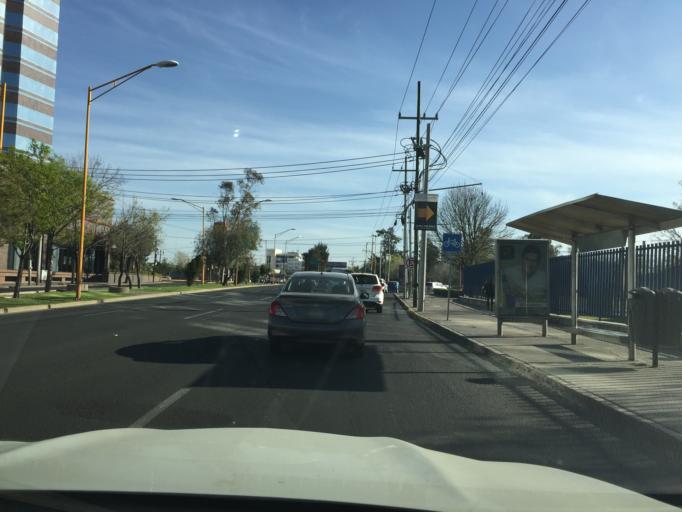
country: MX
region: Aguascalientes
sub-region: Aguascalientes
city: Pocitos
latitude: 21.9177
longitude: -102.3143
